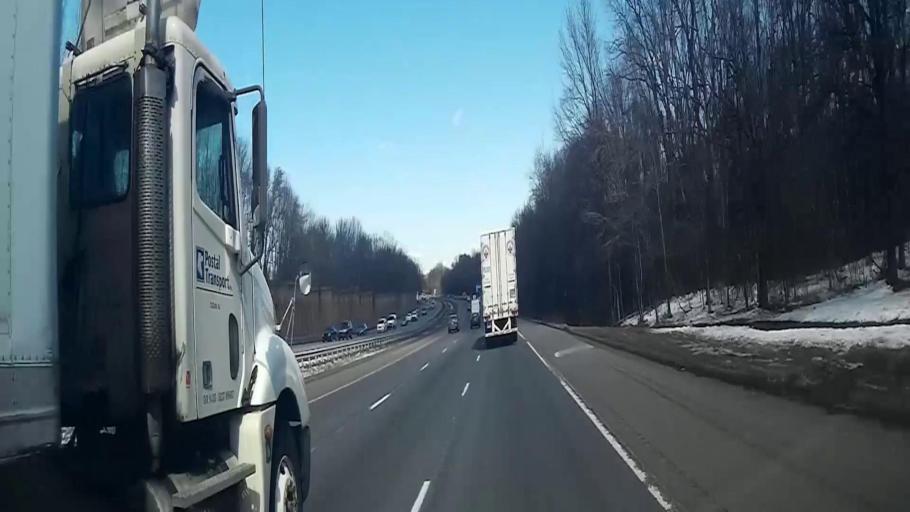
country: US
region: New Jersey
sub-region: Camden County
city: Ellisburg
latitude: 39.8939
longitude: -74.9945
